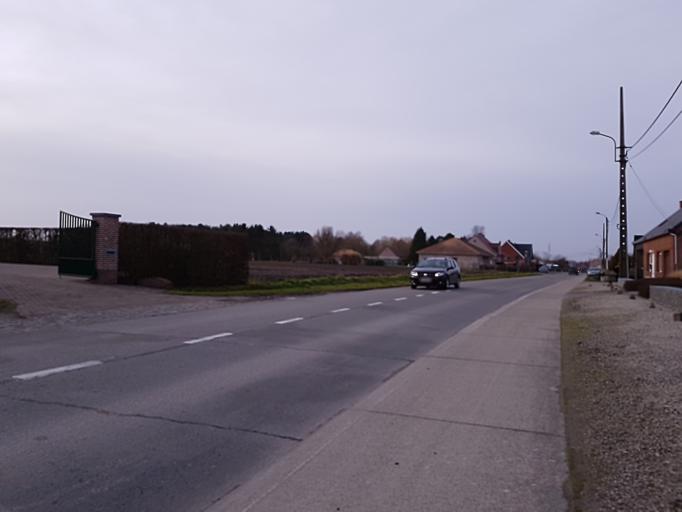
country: BE
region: Flanders
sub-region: Provincie Antwerpen
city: Putte
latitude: 51.0385
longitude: 4.6720
